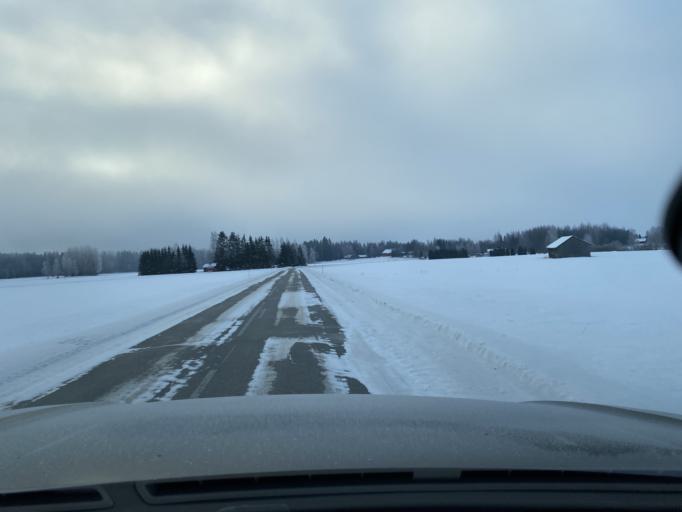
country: FI
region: Haeme
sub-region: Forssa
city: Tammela
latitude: 60.8355
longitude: 23.8380
